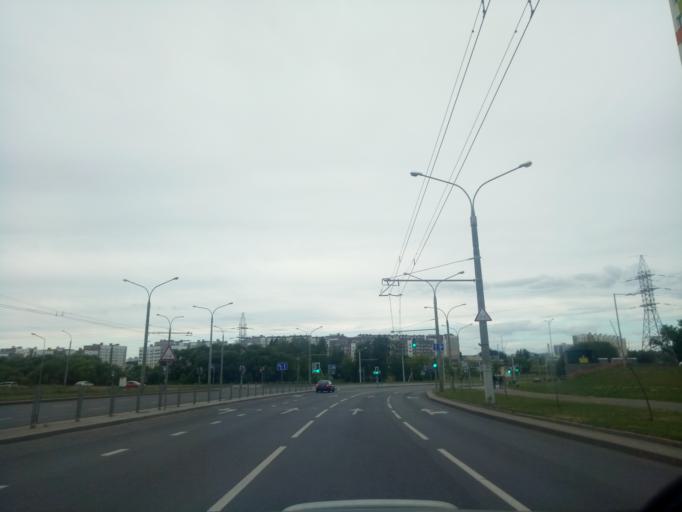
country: BY
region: Minsk
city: Novoye Medvezhino
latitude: 53.8738
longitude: 27.4768
